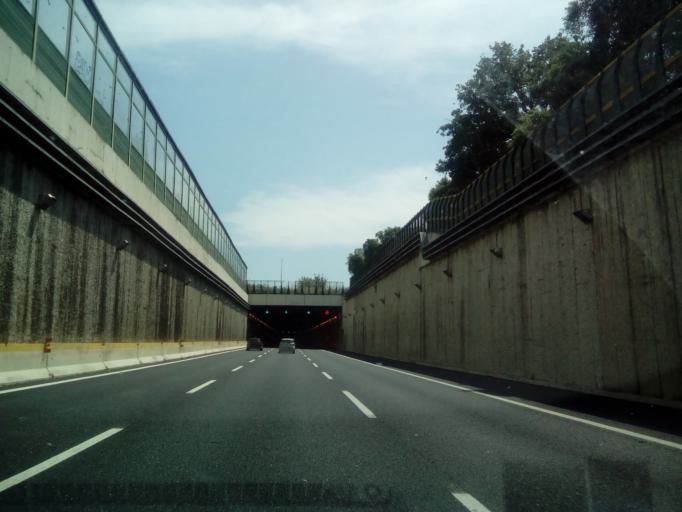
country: IT
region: Latium
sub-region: Citta metropolitana di Roma Capitale
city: Valle Santa
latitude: 41.9475
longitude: 12.3825
